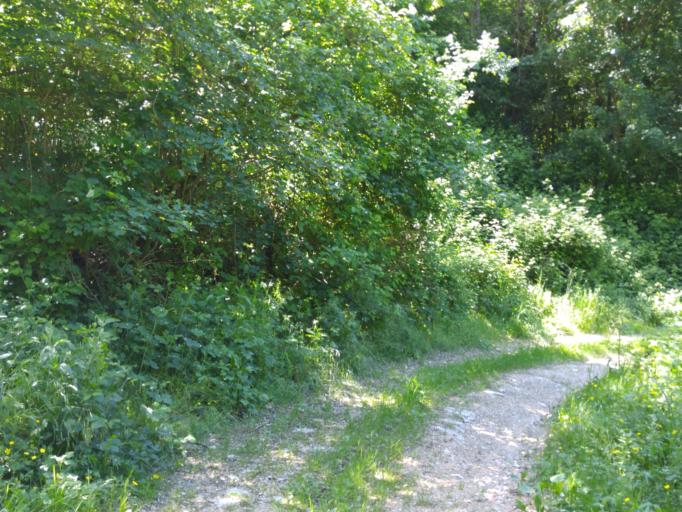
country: IT
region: The Marches
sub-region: Provincia di Pesaro e Urbino
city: Fermignano
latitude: 43.6982
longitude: 12.6326
